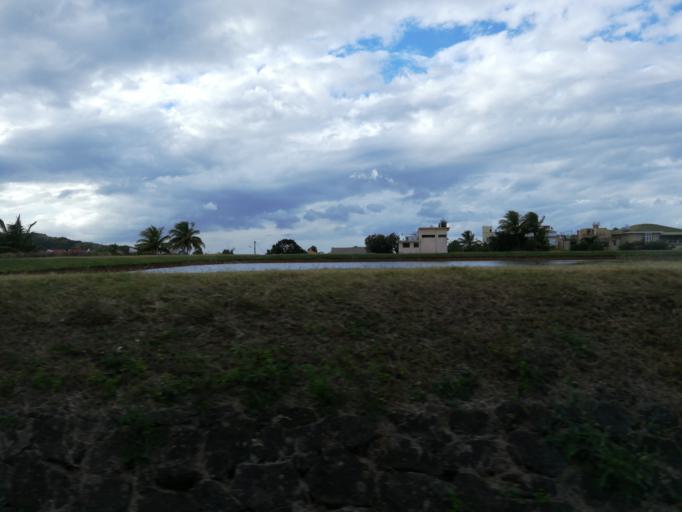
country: MU
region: Plaines Wilhems
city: Quatre Bornes
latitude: -20.2363
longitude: 57.4542
